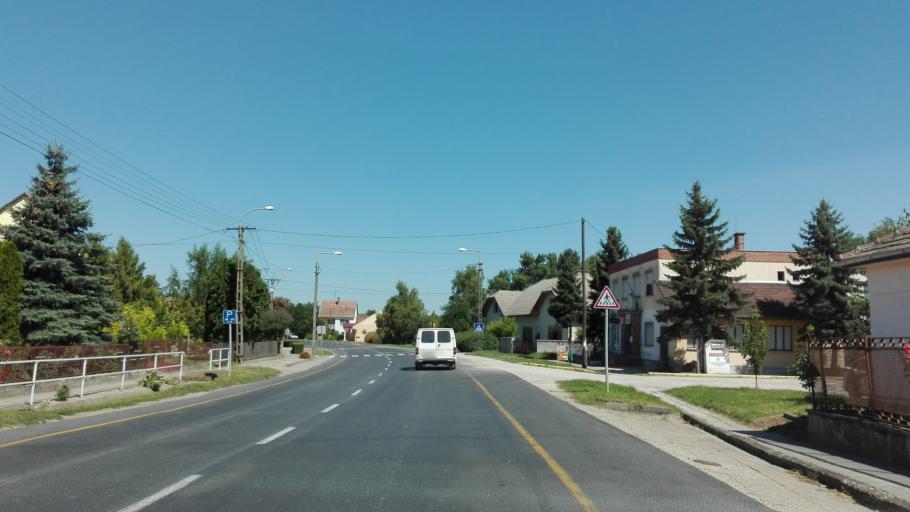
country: HU
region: Fejer
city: Mezoszilas
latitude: 46.8139
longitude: 18.4813
